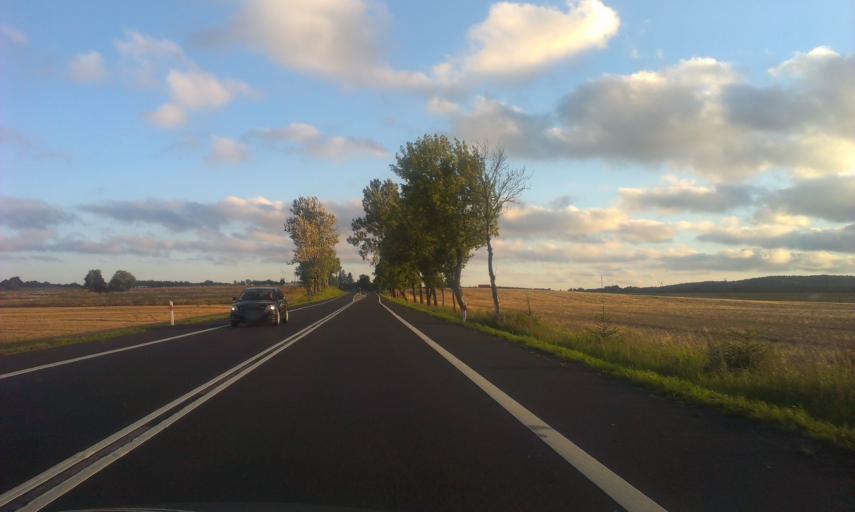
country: PL
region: West Pomeranian Voivodeship
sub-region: Powiat slawienski
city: Darlowo
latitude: 54.2866
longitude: 16.4901
